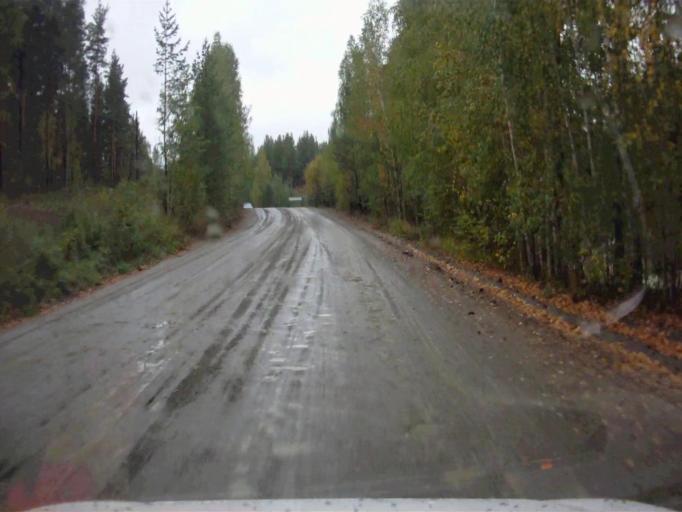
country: RU
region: Chelyabinsk
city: Kyshtym
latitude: 55.7422
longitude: 60.4956
